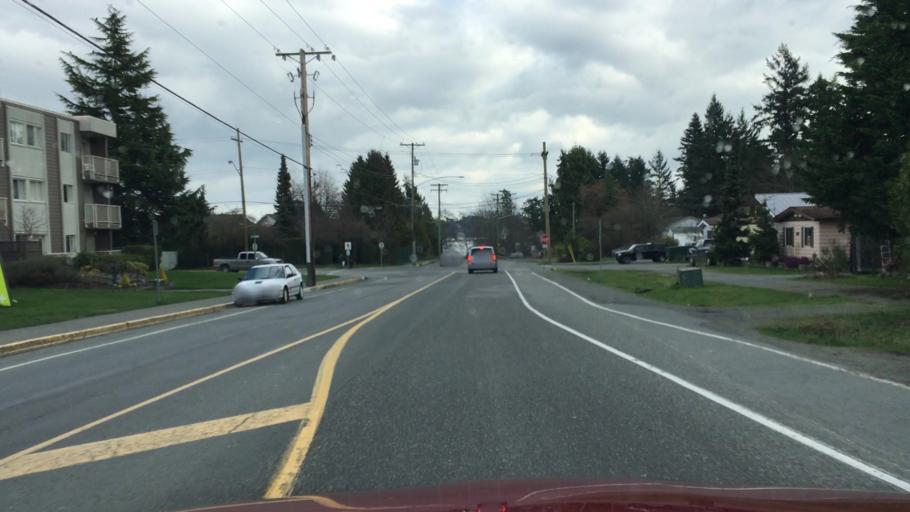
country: CA
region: British Columbia
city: North Saanich
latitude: 48.5941
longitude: -123.3957
